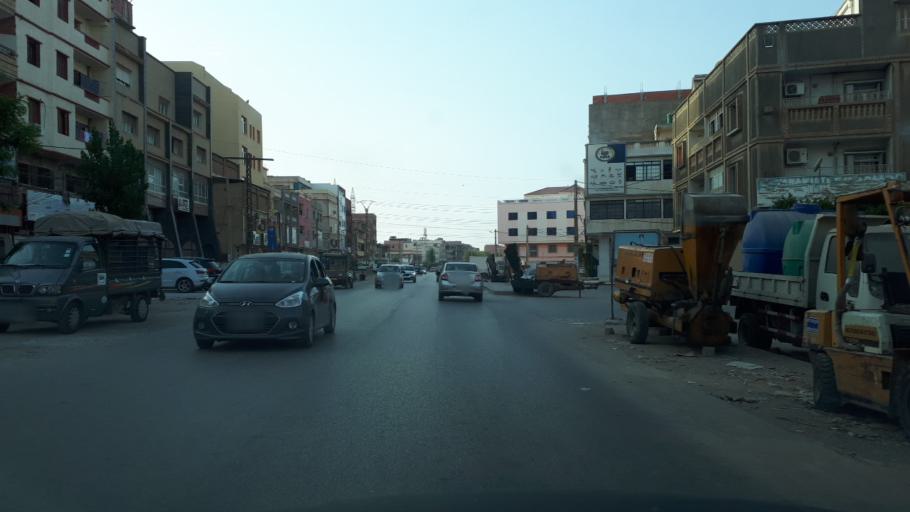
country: DZ
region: Alger
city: Dar el Beida
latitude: 36.7331
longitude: 3.2350
